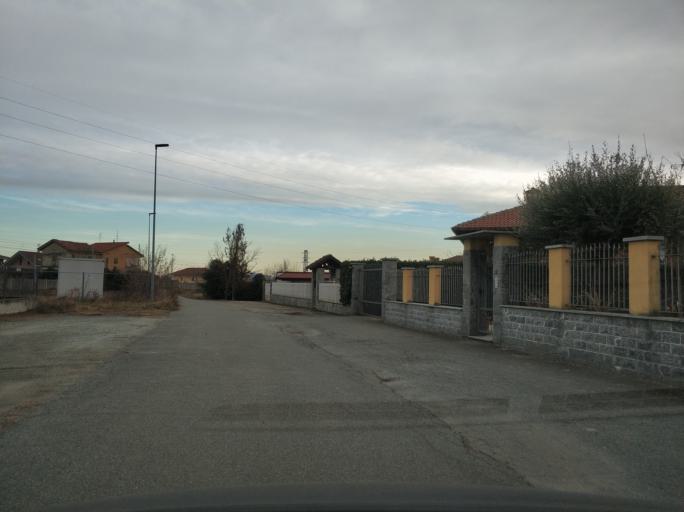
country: IT
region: Piedmont
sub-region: Provincia di Torino
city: San Maurizio
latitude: 45.2114
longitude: 7.6370
